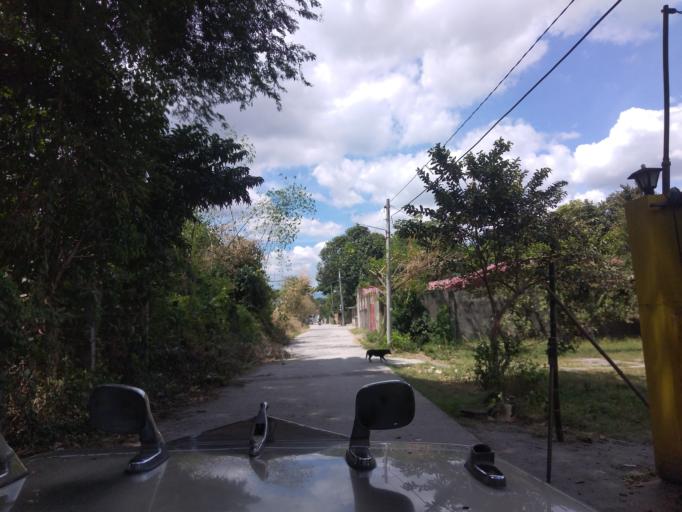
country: PH
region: Central Luzon
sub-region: Province of Pampanga
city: San Basilio
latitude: 15.0157
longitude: 120.5875
